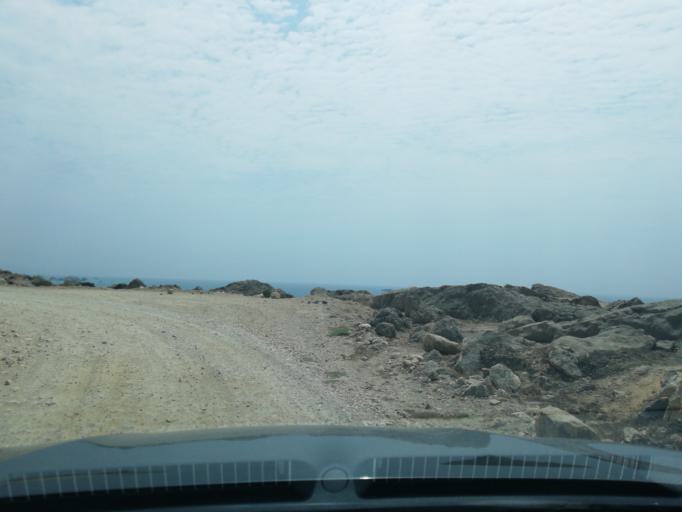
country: OM
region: Zufar
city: Salalah
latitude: 16.8175
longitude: 53.6938
